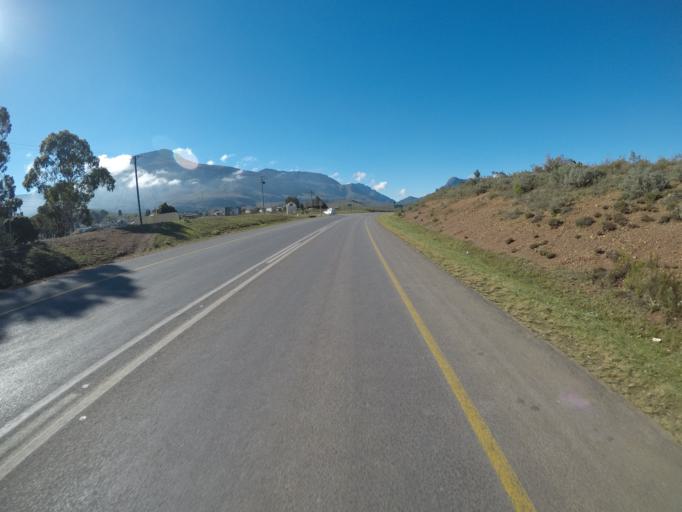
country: ZA
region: Western Cape
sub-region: Overberg District Municipality
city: Caledon
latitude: -34.0496
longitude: 19.5641
